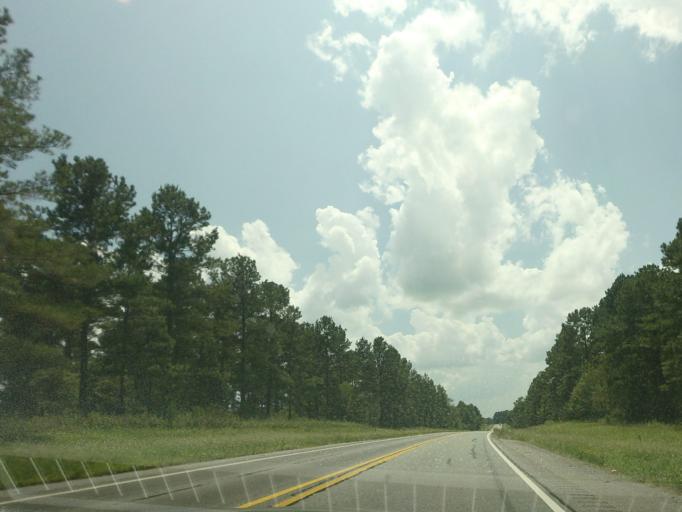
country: US
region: Georgia
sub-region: Bleckley County
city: Cochran
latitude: 32.3818
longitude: -83.3282
